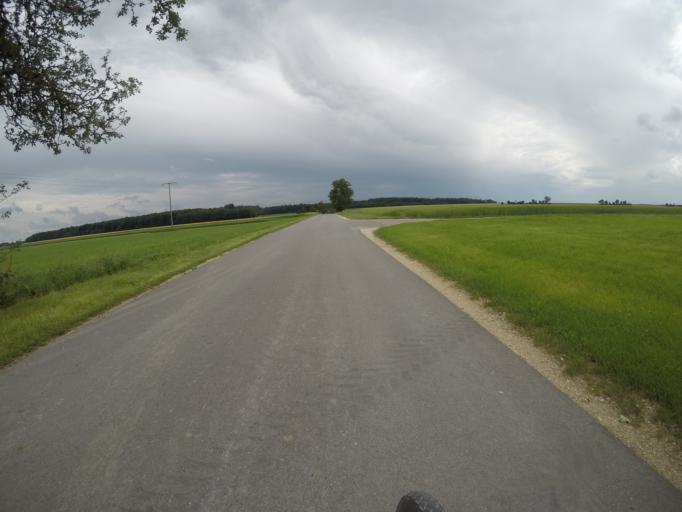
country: DE
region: Baden-Wuerttemberg
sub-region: Tuebingen Region
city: Dornstadt
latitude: 48.4902
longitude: 9.9521
